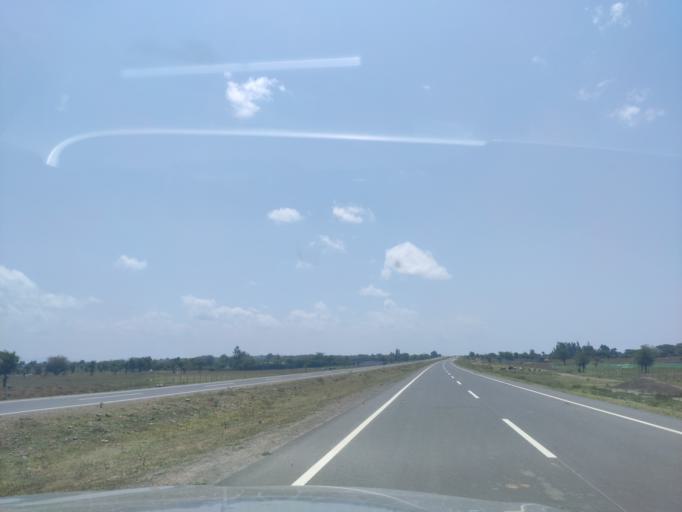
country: ET
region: Oromiya
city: Mojo
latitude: 8.3390
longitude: 38.9704
